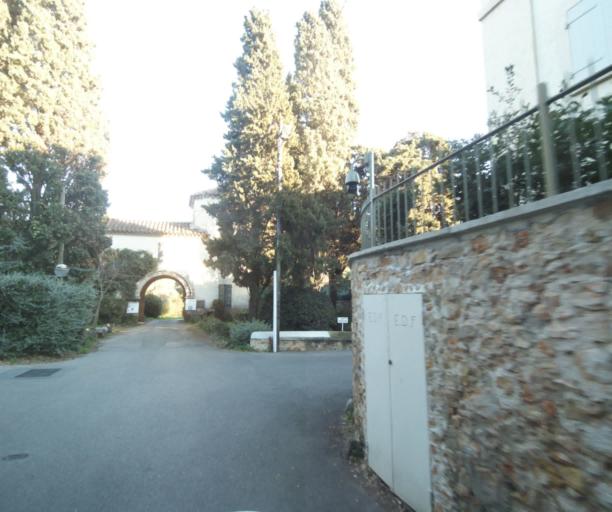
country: FR
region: Provence-Alpes-Cote d'Azur
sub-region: Departement des Alpes-Maritimes
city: Antibes
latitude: 43.5492
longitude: 7.1320
